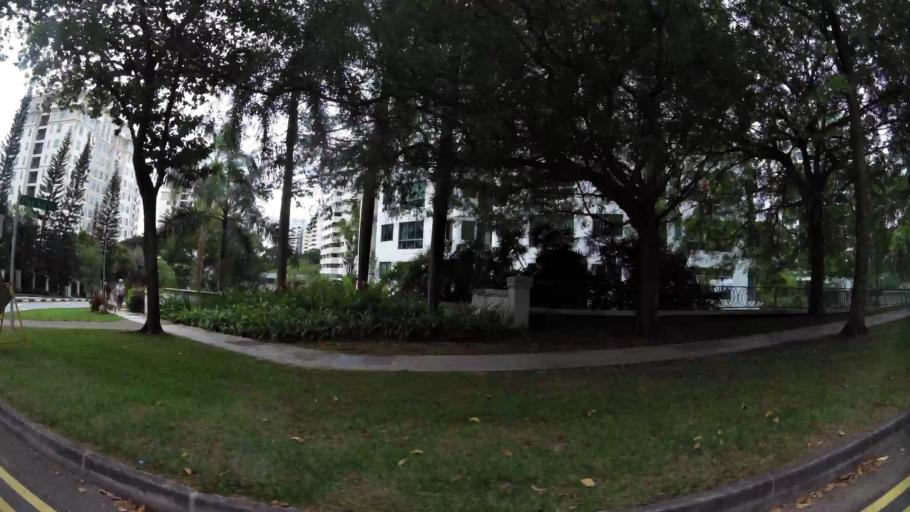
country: SG
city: Singapore
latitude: 1.3173
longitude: 103.7770
